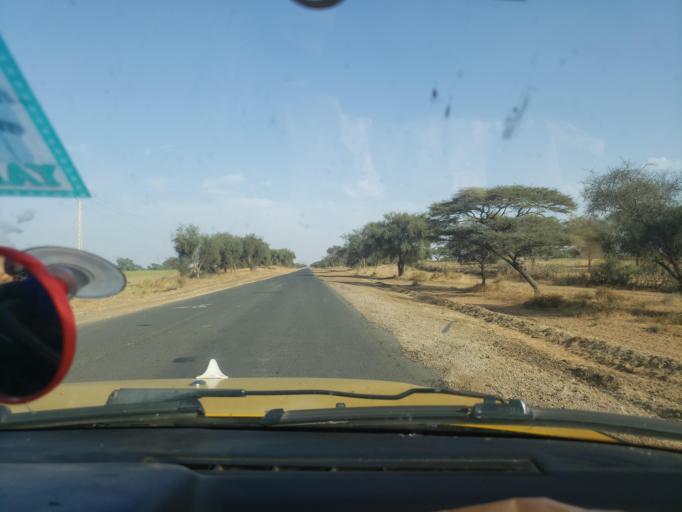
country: SN
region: Louga
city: Louga
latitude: 15.5079
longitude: -15.9715
